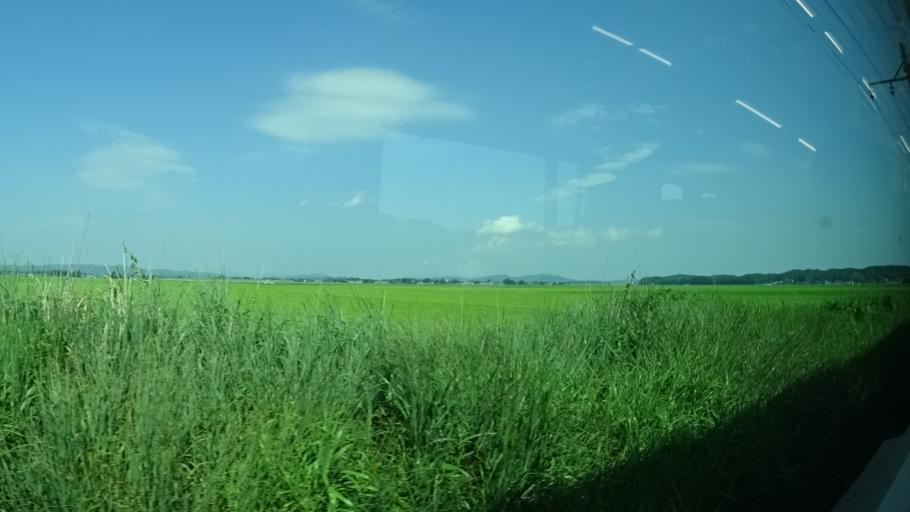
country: JP
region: Miyagi
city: Kogota
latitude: 38.5113
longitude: 141.0762
